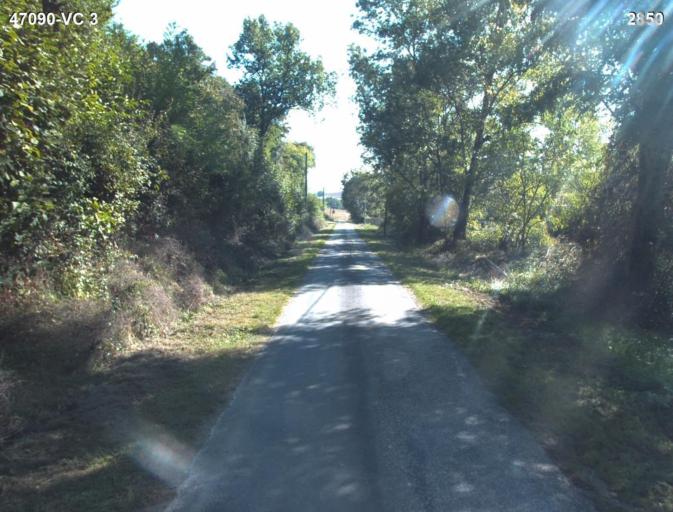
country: FR
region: Aquitaine
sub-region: Departement du Lot-et-Garonne
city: Nerac
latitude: 44.1716
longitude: 0.3862
